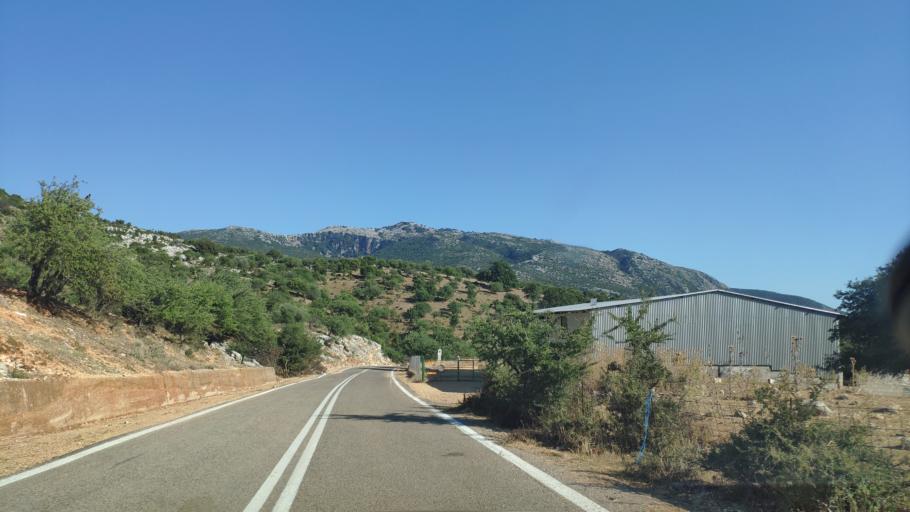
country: GR
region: West Greece
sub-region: Nomos Aitolias kai Akarnanias
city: Archontochorion
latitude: 38.6924
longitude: 21.0601
